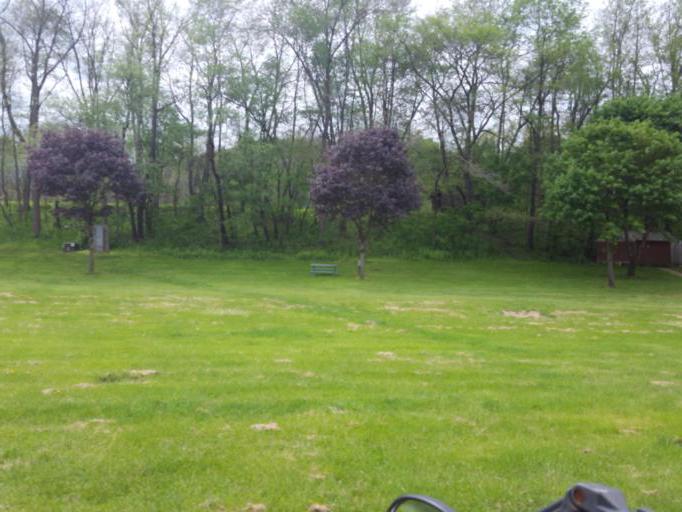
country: US
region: Ohio
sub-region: Ashland County
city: Loudonville
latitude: 40.5495
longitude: -82.1986
